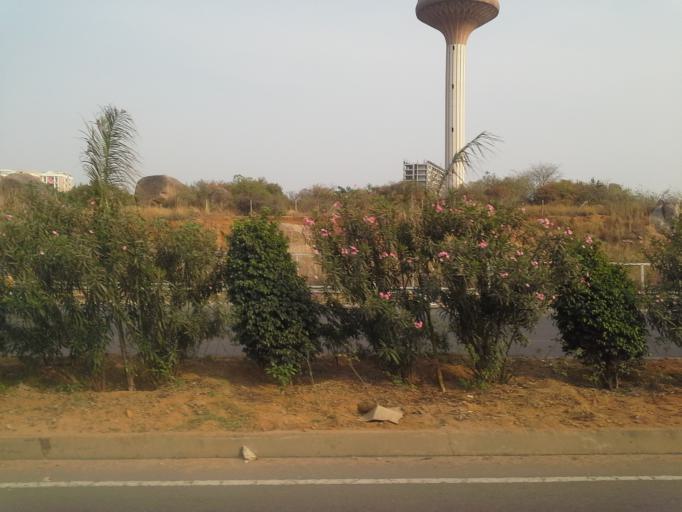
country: IN
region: Telangana
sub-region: Rangareddi
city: Kukatpalli
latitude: 17.4310
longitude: 78.3593
